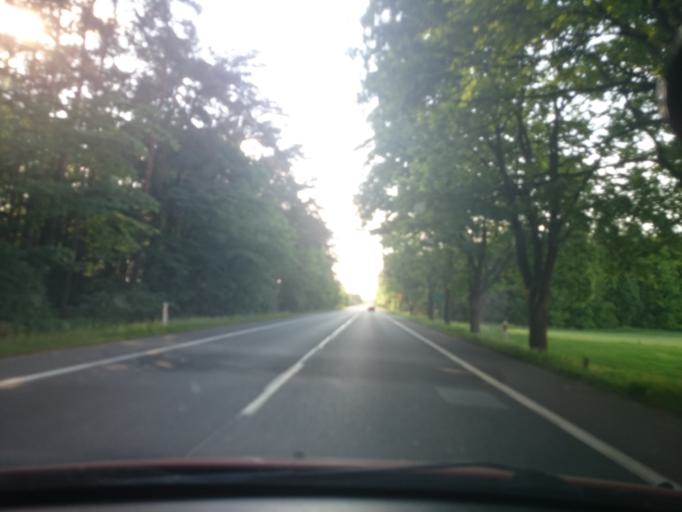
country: PL
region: Opole Voivodeship
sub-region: Powiat strzelecki
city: Strzelce Opolskie
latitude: 50.5473
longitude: 18.2321
